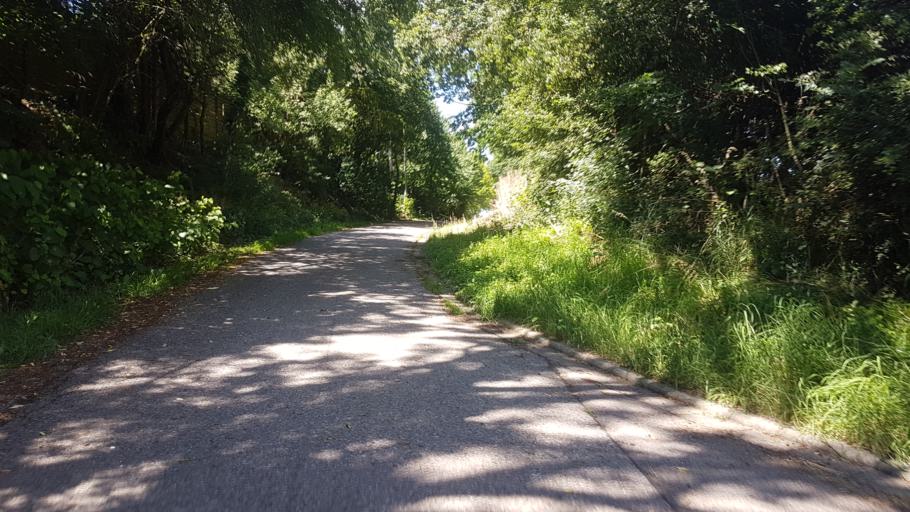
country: DE
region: Bavaria
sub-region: Regierungsbezirk Mittelfranken
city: Leutershausen
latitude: 49.3089
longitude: 10.3914
